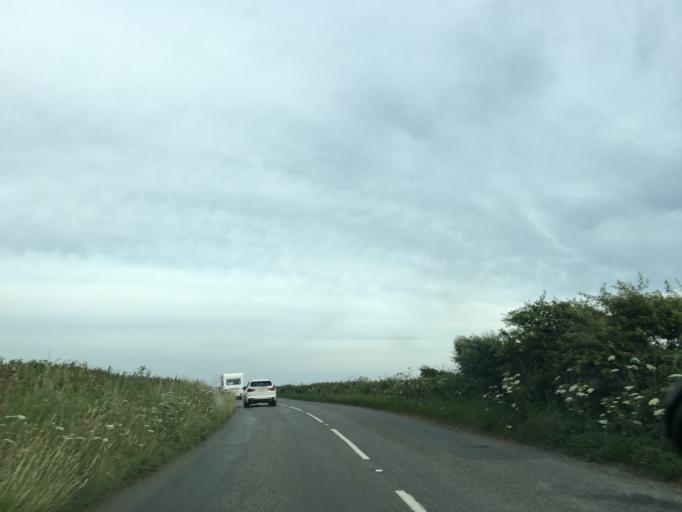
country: GB
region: England
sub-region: Isle of Wight
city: Shalfleet
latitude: 50.6436
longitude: -1.4371
